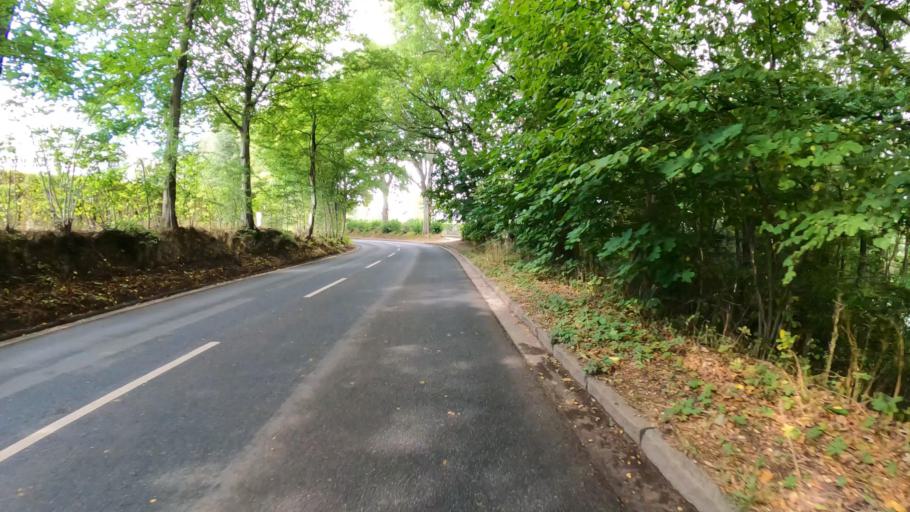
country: DE
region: Hamburg
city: Lemsahl-Mellingstedt
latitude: 53.6866
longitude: 10.1117
